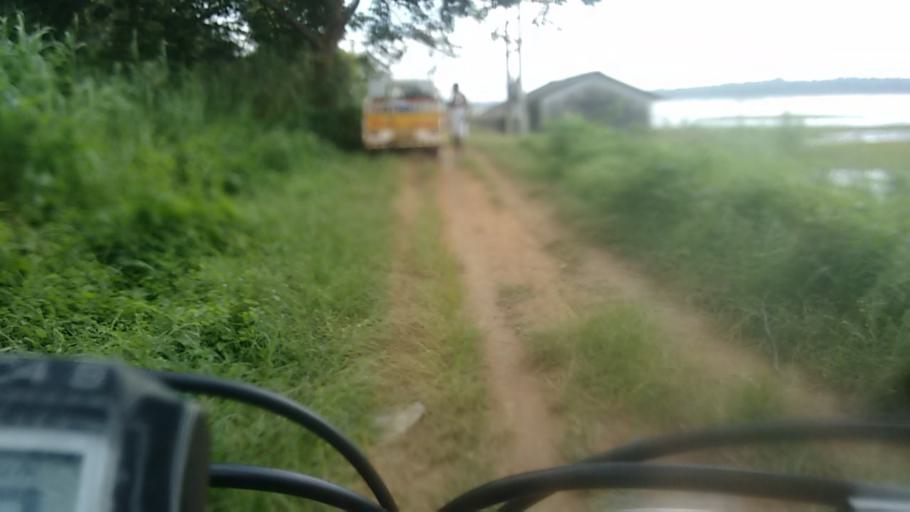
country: IN
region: Kerala
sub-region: Thrissur District
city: Trichur
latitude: 10.5310
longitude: 76.1572
